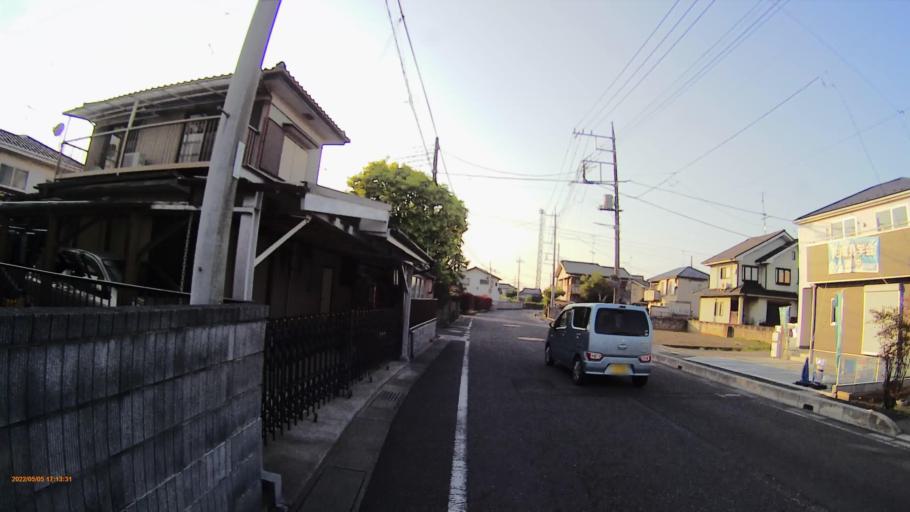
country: JP
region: Saitama
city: Kurihashi
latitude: 36.1270
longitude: 139.7091
